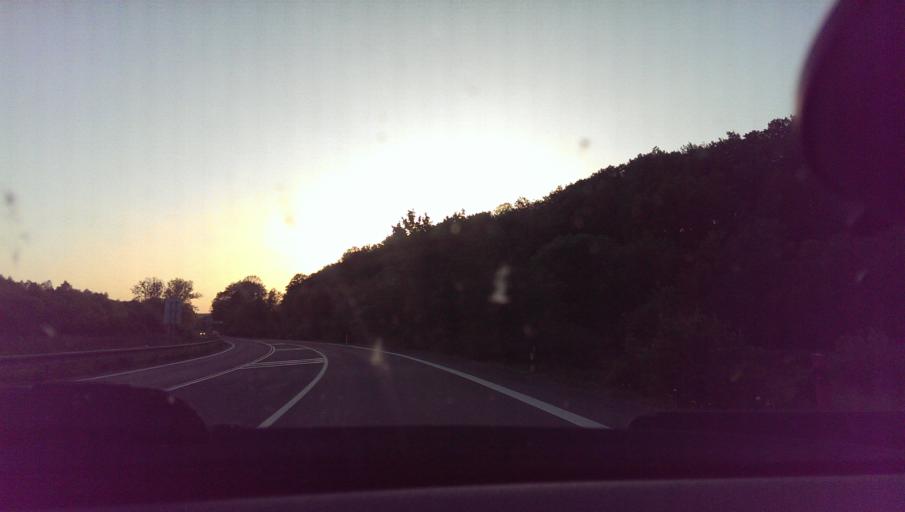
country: CZ
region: Zlin
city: Valasske Mezirici
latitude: 49.4763
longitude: 18.0025
